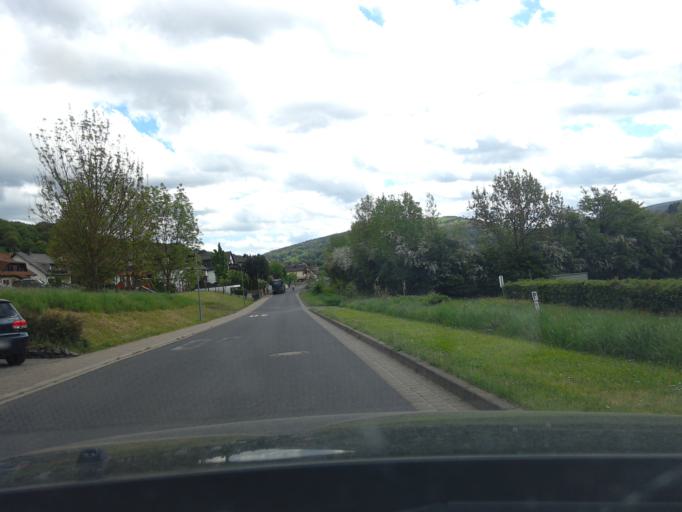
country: DE
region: Hesse
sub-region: Regierungsbezirk Darmstadt
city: Bad Orb
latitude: 50.2363
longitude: 9.3317
